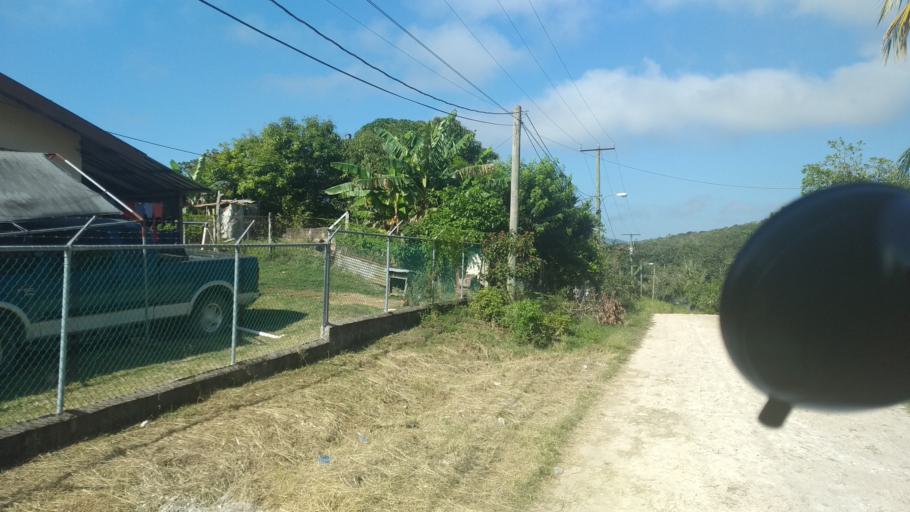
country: BZ
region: Cayo
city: Benque Viejo del Carmen
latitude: 17.0836
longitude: -89.1324
